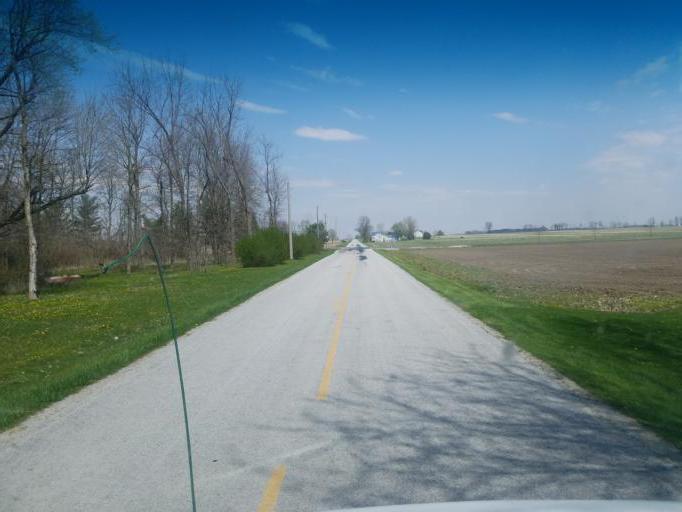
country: US
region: Ohio
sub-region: Hardin County
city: Forest
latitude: 40.7442
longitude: -83.5378
